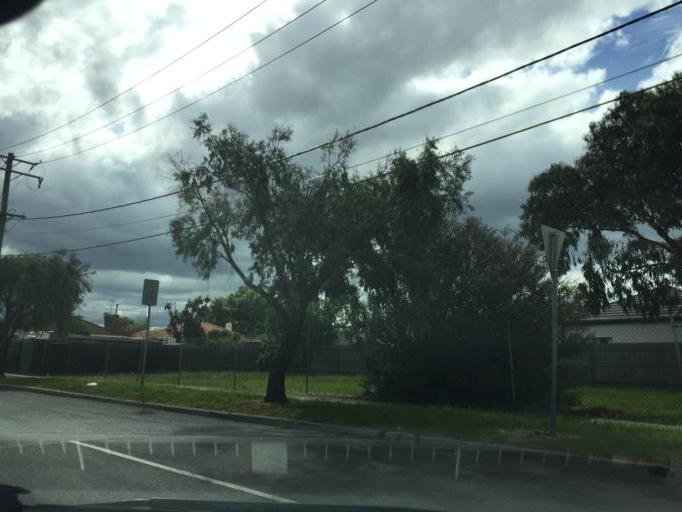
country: AU
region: Victoria
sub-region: Maribyrnong
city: West Footscray
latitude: -37.8013
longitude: 144.8619
